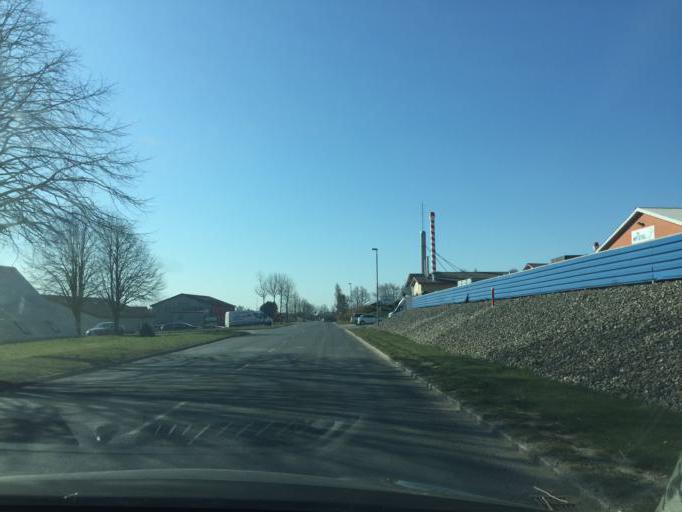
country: DK
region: South Denmark
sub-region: Faaborg-Midtfyn Kommune
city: Ringe
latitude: 55.2504
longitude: 10.4855
